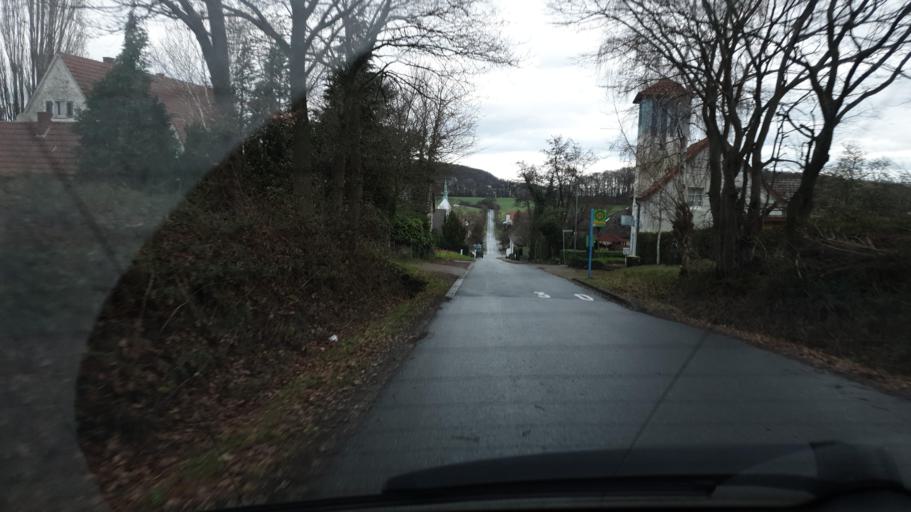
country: DE
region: North Rhine-Westphalia
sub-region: Regierungsbezirk Detmold
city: Vlotho
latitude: 52.1595
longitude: 8.8279
